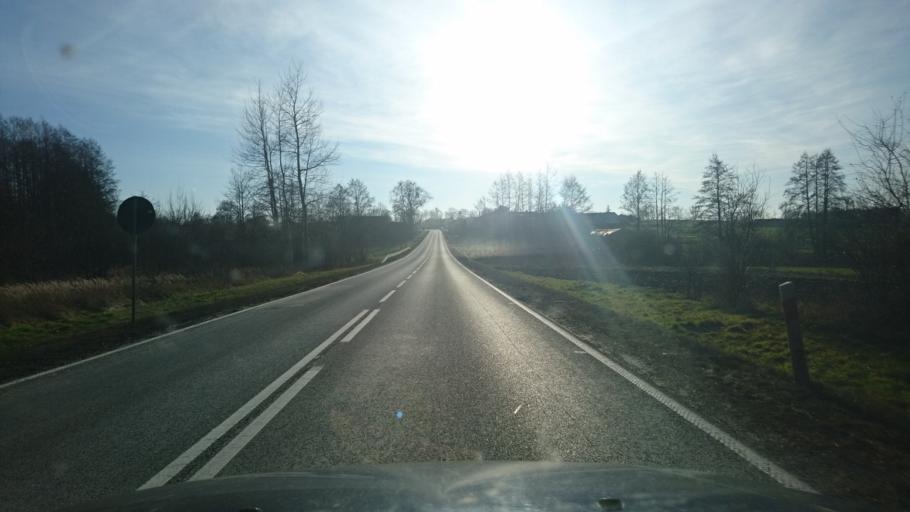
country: PL
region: Opole Voivodeship
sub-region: Powiat oleski
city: Dalachow
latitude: 51.0475
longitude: 18.5971
